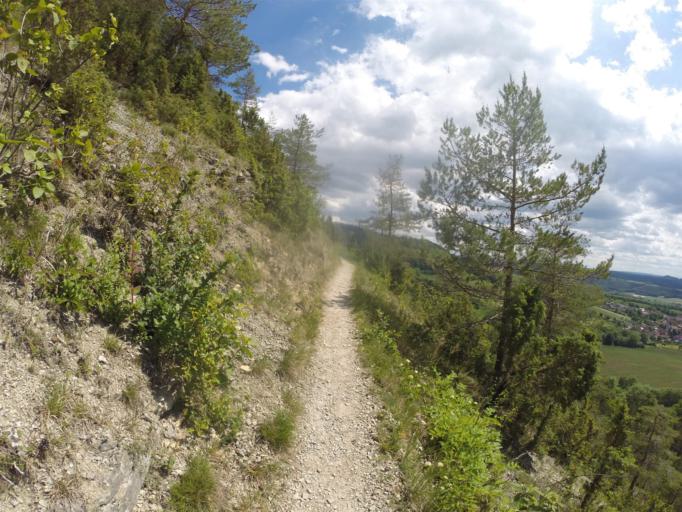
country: DE
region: Thuringia
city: Zollnitz
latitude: 50.8956
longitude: 11.6346
